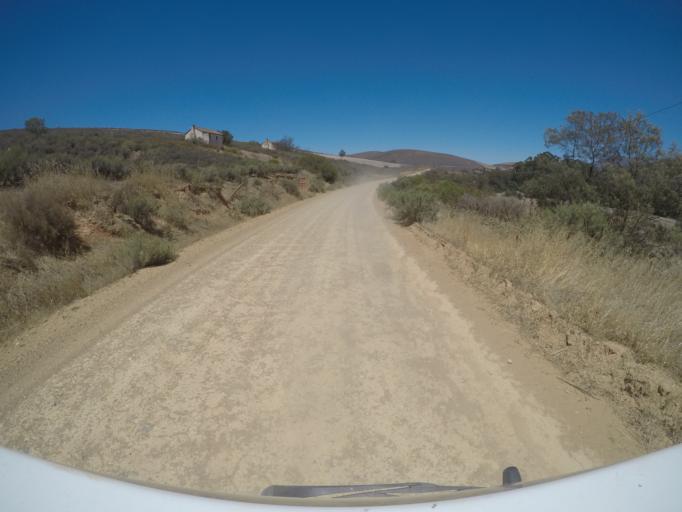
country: ZA
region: Western Cape
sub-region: Overberg District Municipality
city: Caledon
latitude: -34.1389
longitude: 19.2481
